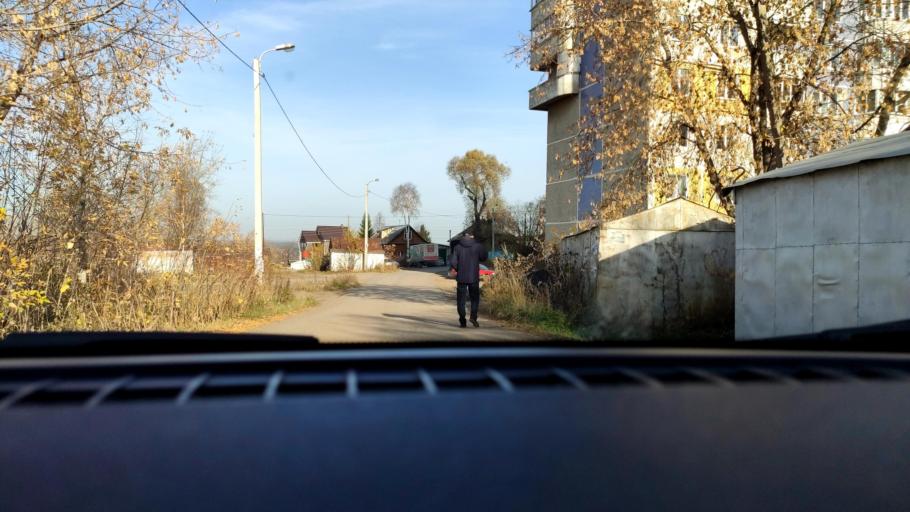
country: RU
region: Perm
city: Perm
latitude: 58.0325
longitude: 56.3191
